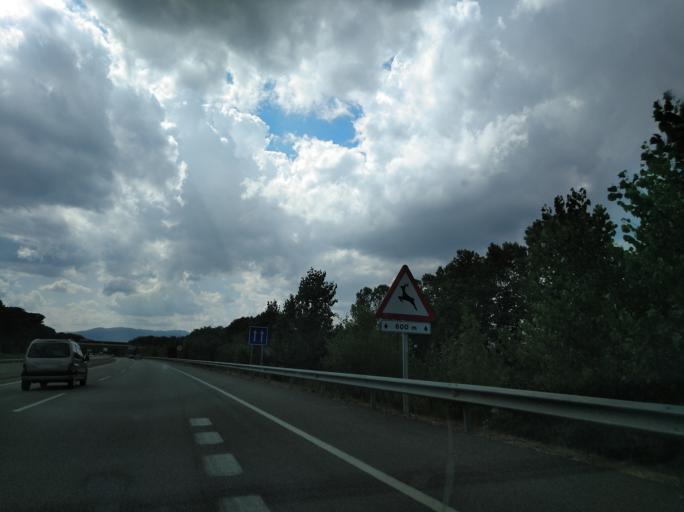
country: ES
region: Catalonia
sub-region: Provincia de Girona
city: Vilobi d'Onyar
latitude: 41.8753
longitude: 2.7560
